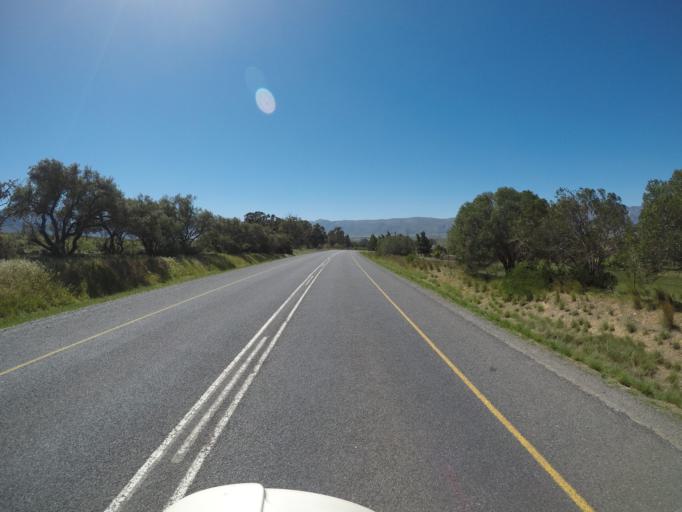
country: ZA
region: Western Cape
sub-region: Cape Winelands District Municipality
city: Ceres
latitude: -33.3137
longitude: 19.0945
